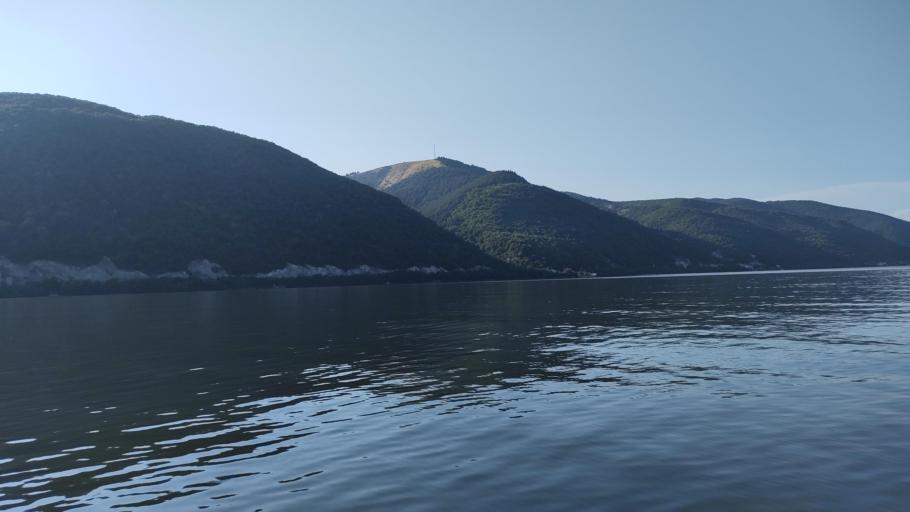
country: RO
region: Mehedinti
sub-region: Comuna Dubova
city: Dubova
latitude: 44.5441
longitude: 22.2220
